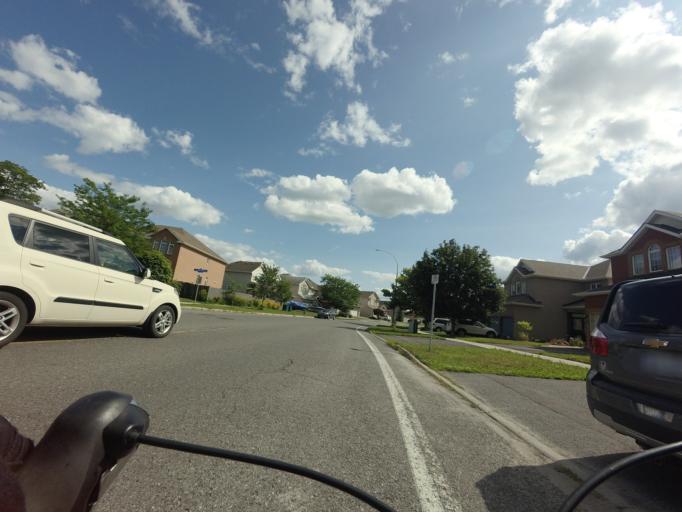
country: CA
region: Ontario
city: Bells Corners
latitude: 45.2979
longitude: -75.8530
